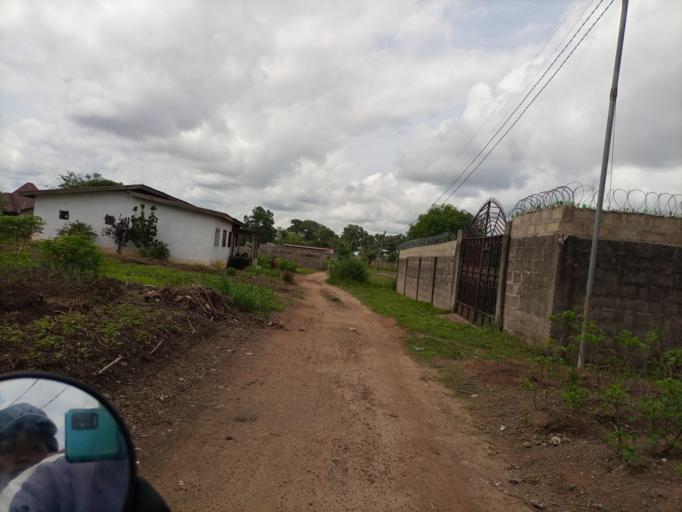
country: SL
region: Southern Province
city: Bo
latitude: 7.9733
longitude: -11.7573
